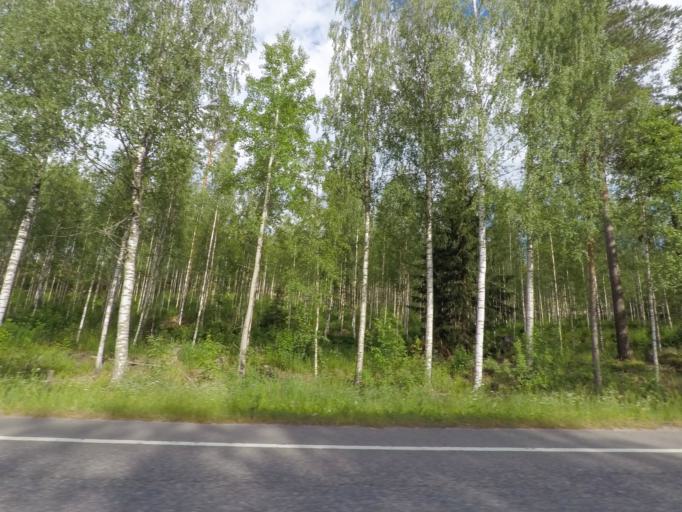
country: FI
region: Uusimaa
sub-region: Porvoo
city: Pukkila
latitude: 60.8090
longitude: 25.4809
